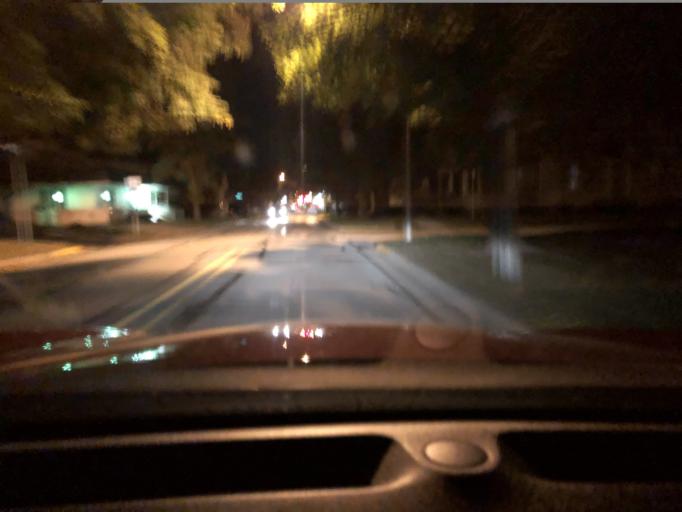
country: US
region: Indiana
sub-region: DeKalb County
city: Auburn
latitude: 41.3700
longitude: -85.0560
